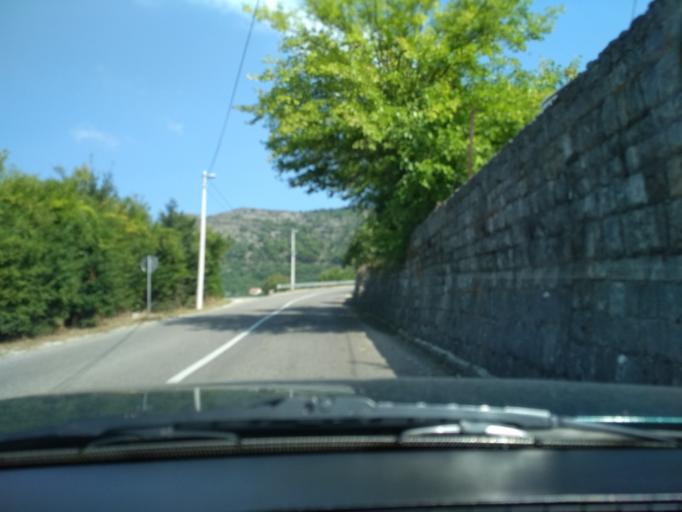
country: ME
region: Kotor
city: Kotor
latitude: 42.3969
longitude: 18.7556
